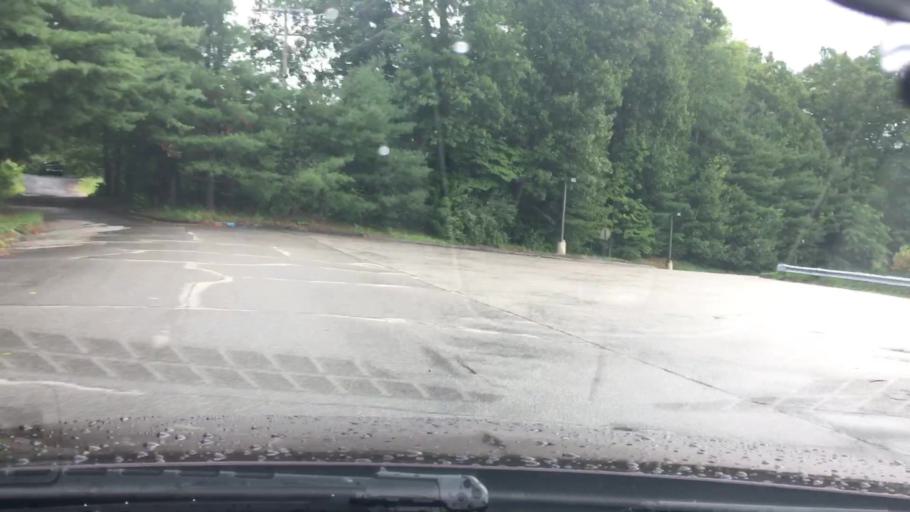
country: US
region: Connecticut
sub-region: Hartford County
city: Glastonbury Center
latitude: 41.7097
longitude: -72.5769
